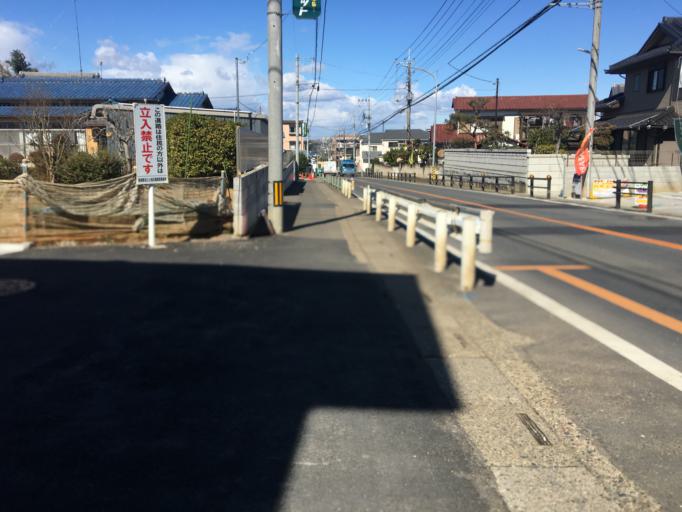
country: JP
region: Saitama
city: Shiki
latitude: 35.8083
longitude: 139.5539
